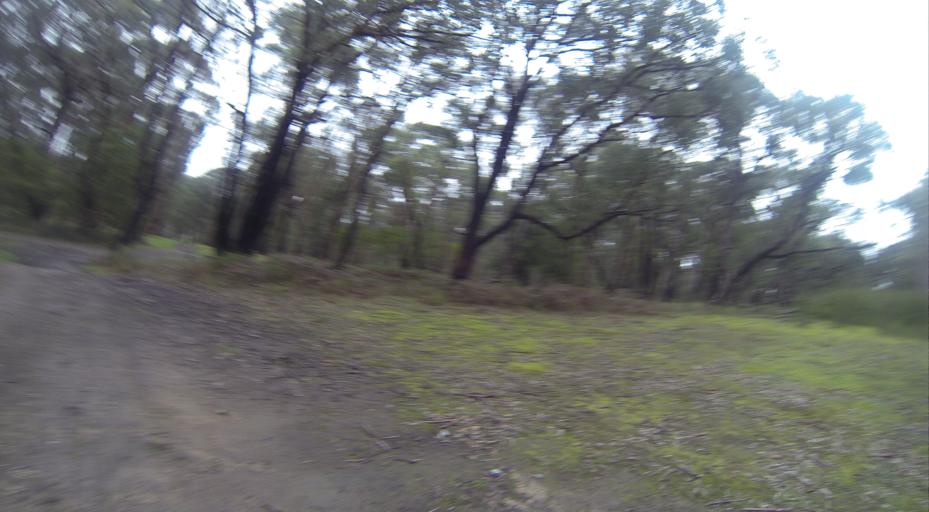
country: AU
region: Victoria
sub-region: Yarra Ranges
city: Lysterfield
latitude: -37.9377
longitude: 145.2993
